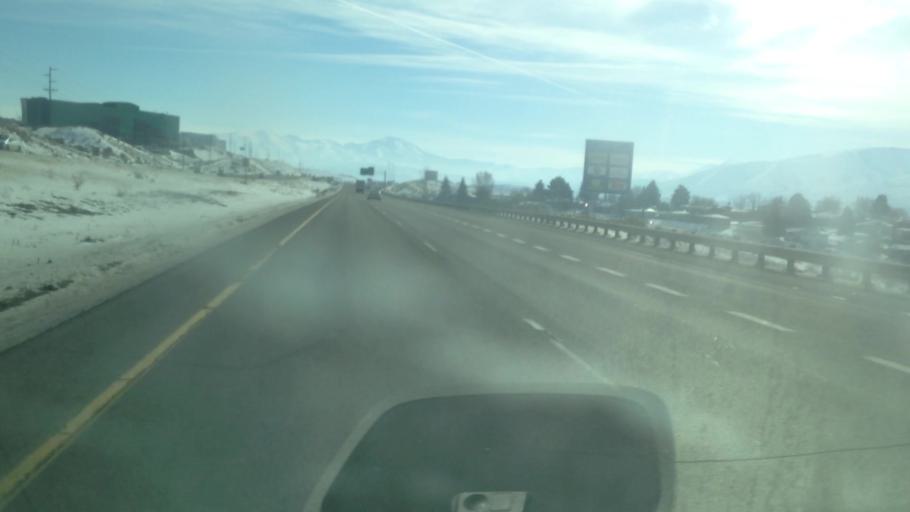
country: US
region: Idaho
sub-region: Bannock County
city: Pocatello
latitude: 42.8860
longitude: -112.4301
